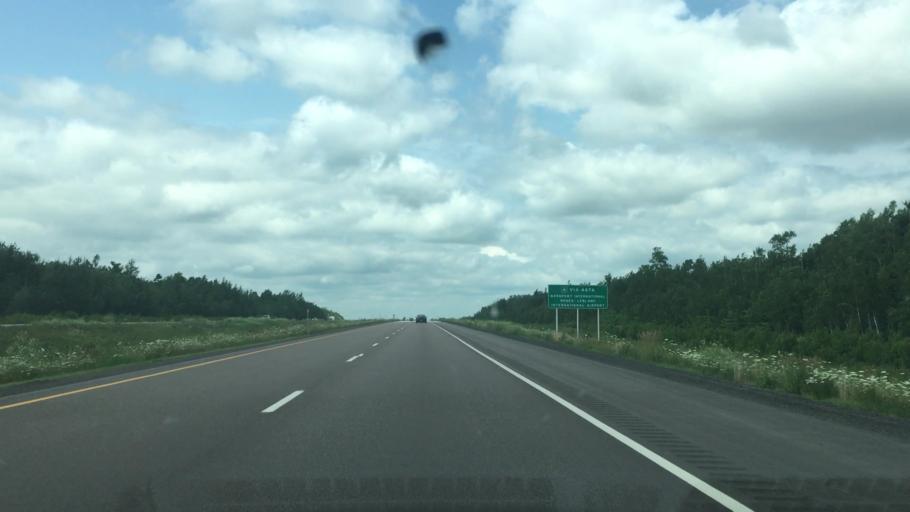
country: CA
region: New Brunswick
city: Dieppe
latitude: 46.1189
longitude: -64.6269
